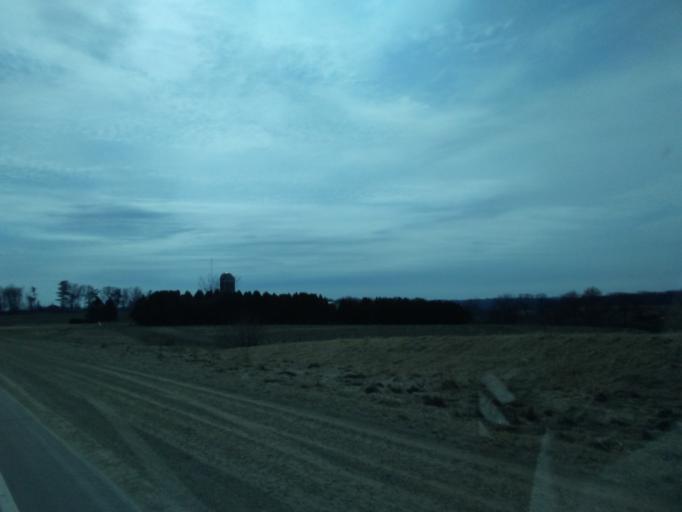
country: US
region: Iowa
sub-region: Winneshiek County
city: Decorah
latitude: 43.3547
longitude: -91.8048
